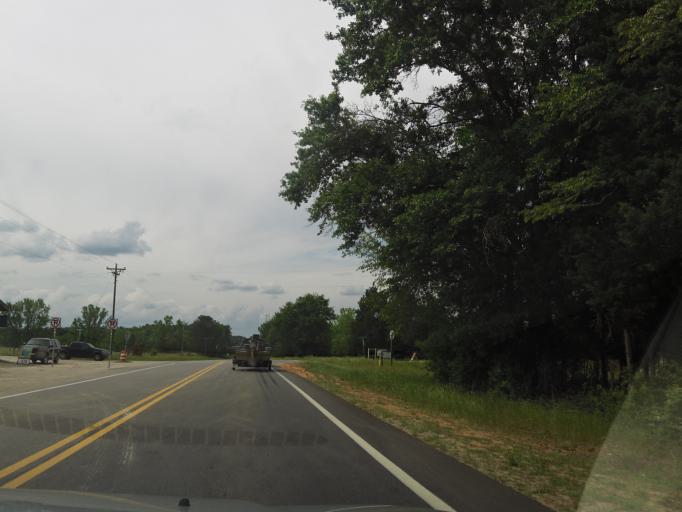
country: US
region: Georgia
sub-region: McDuffie County
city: Thomson
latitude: 33.3641
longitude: -82.4657
